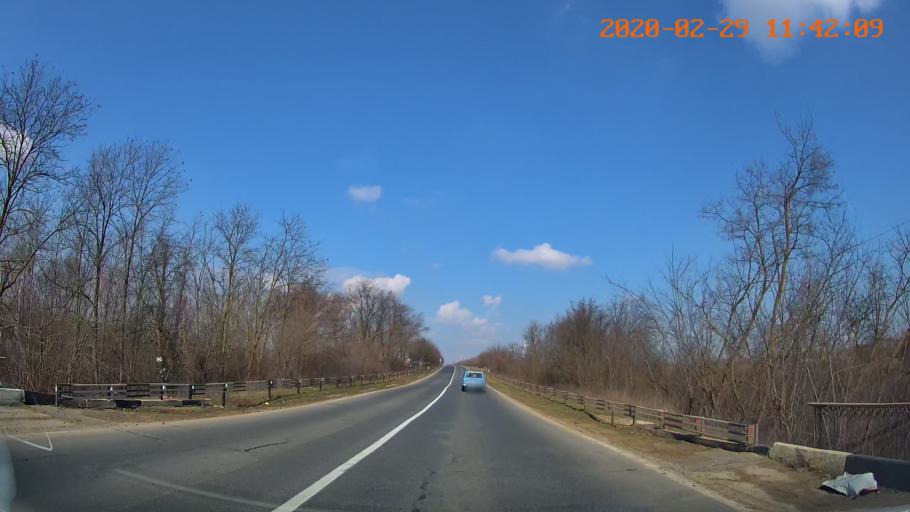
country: MD
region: Rezina
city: Saharna
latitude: 47.6802
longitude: 29.0141
